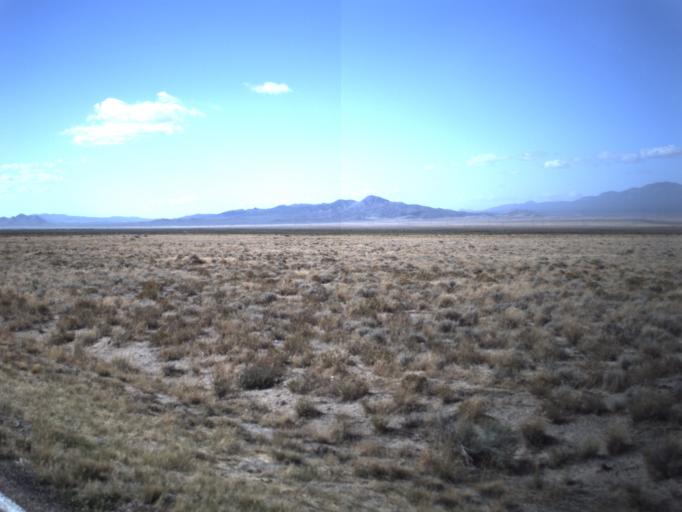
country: US
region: Utah
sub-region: Beaver County
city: Milford
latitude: 38.6506
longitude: -112.9825
